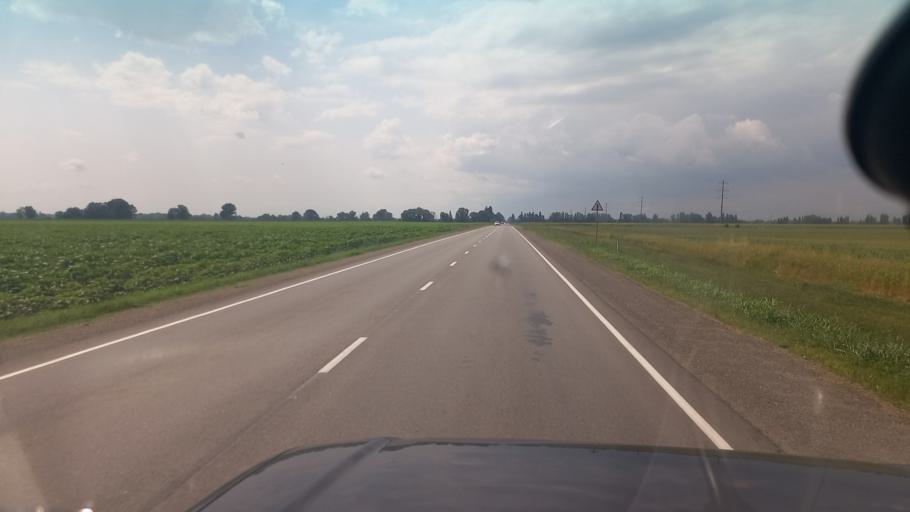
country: RU
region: Adygeya
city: Koshekhabl'
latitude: 44.9071
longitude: 40.4603
